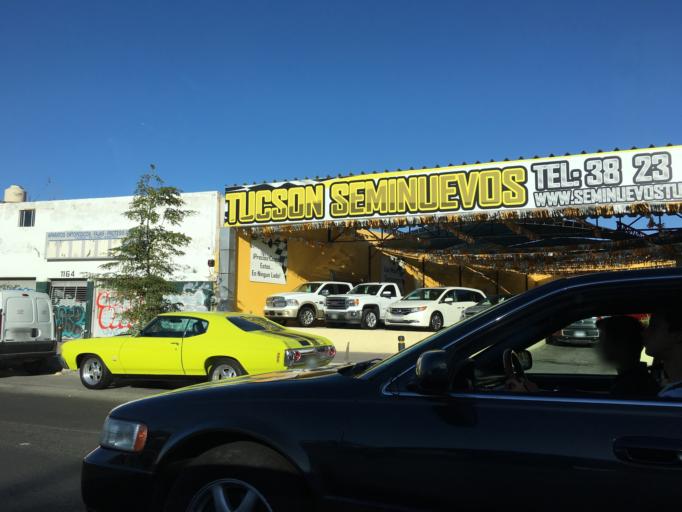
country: MX
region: Jalisco
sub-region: Zapopan
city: Zapopan
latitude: 20.6937
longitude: -103.3540
